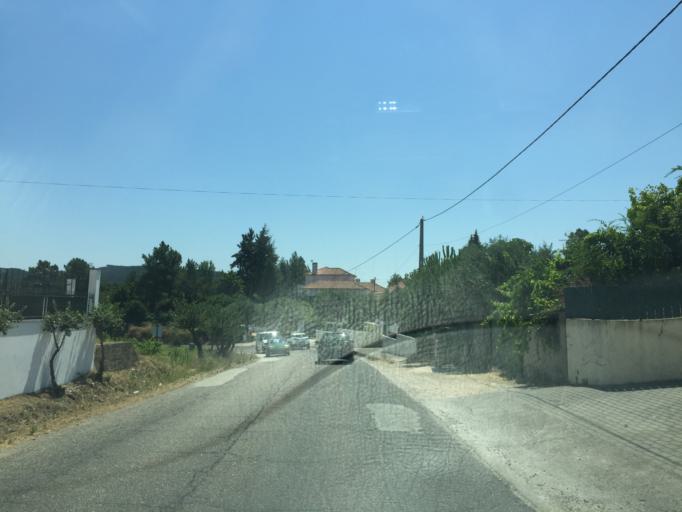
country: PT
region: Santarem
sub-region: Tomar
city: Tomar
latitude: 39.5947
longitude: -8.3697
